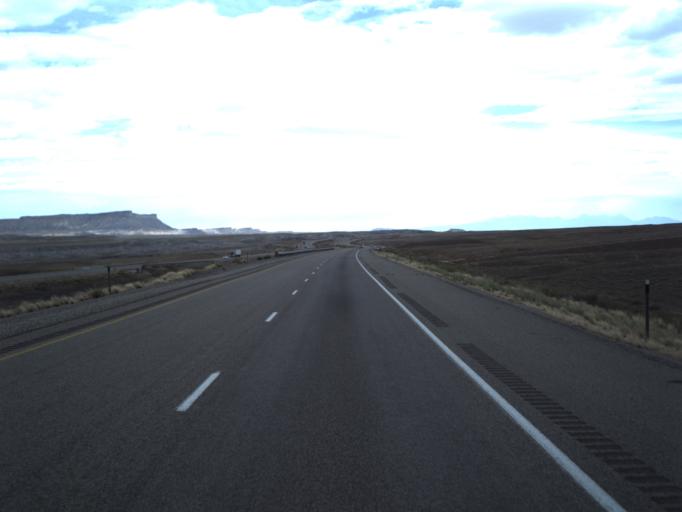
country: US
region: Utah
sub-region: Grand County
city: Moab
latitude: 38.9664
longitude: -110.0824
